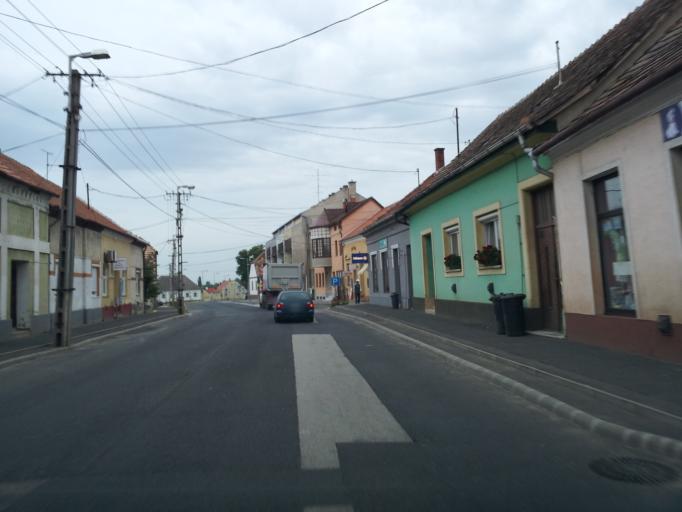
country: HU
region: Veszprem
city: Devecser
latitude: 47.1043
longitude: 17.4369
